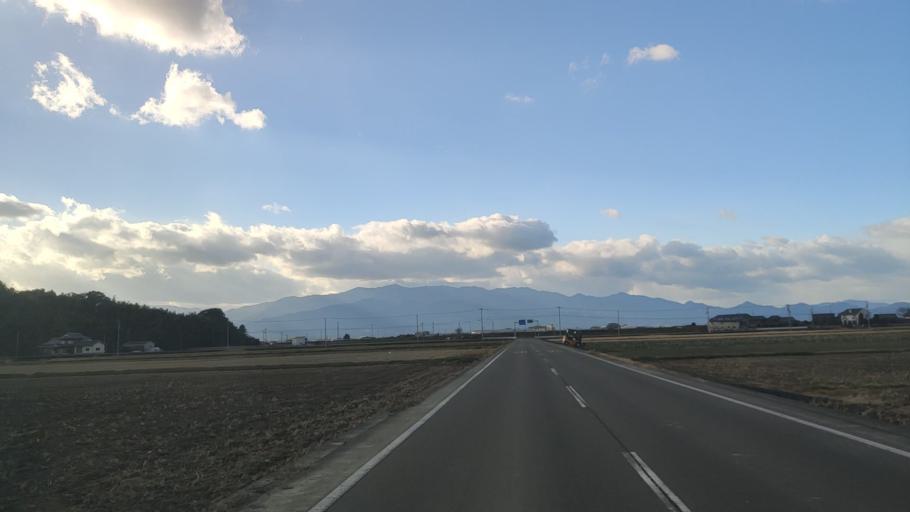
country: JP
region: Ehime
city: Saijo
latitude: 33.9039
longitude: 133.1322
